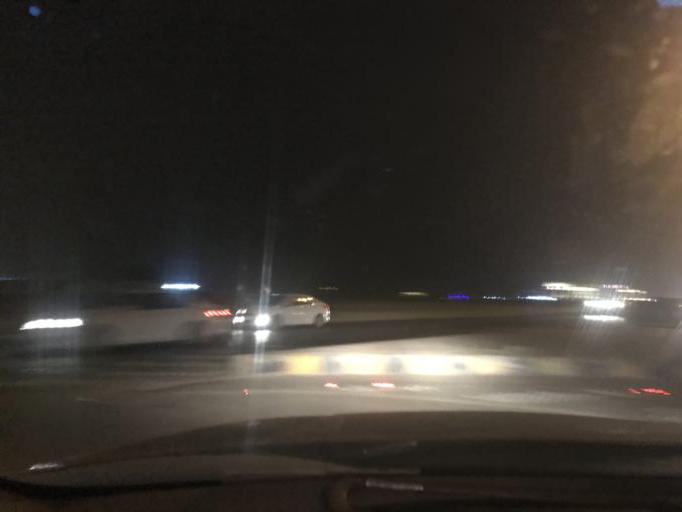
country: SA
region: Ar Riyad
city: Riyadh
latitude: 24.8357
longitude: 46.7384
